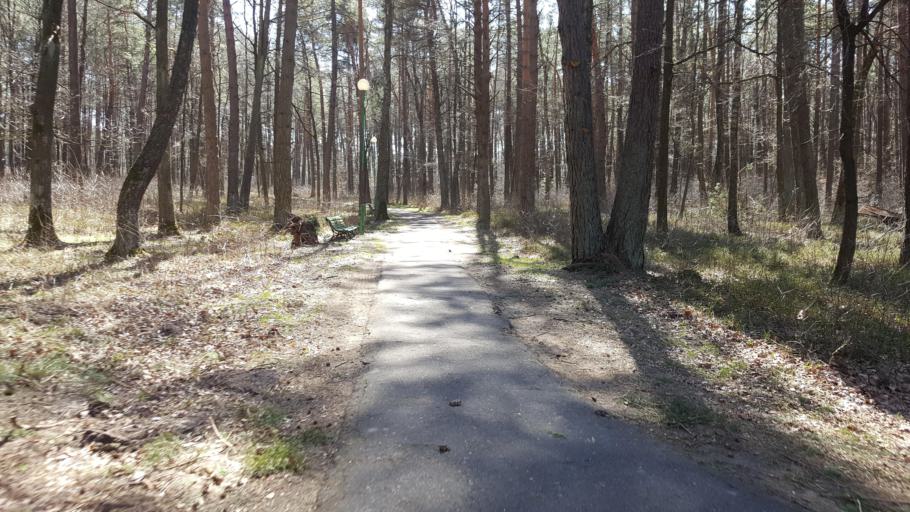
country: BY
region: Brest
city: Kamyanyets
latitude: 52.3527
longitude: 23.8236
